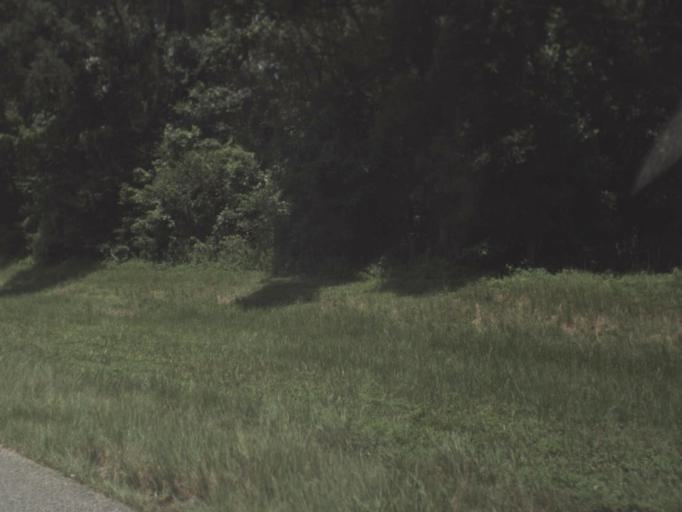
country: US
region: Florida
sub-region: Hernando County
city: North Brooksville
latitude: 28.6196
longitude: -82.4128
